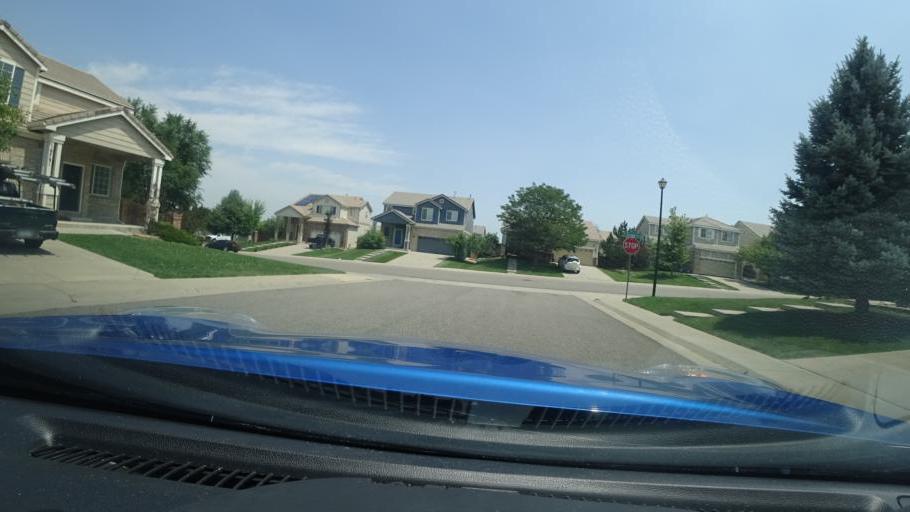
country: US
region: Colorado
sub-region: Adams County
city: Aurora
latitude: 39.6742
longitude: -104.7562
